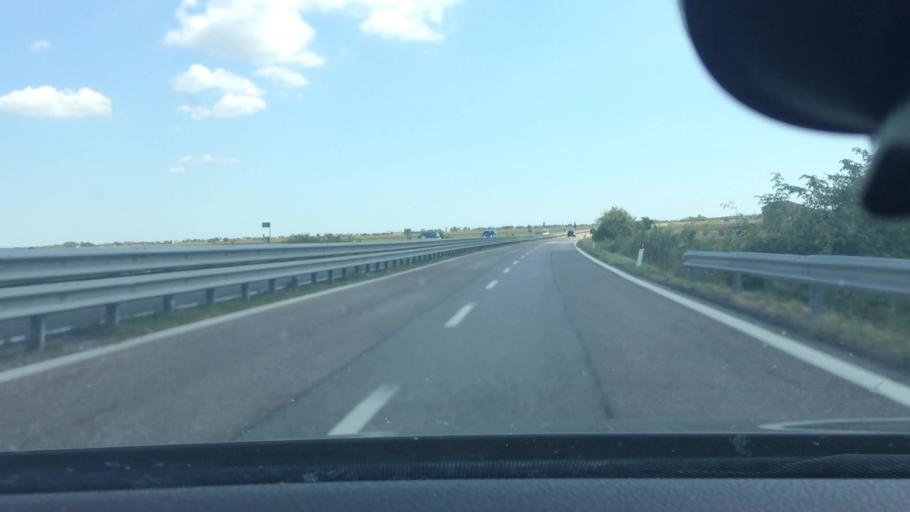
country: IT
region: Emilia-Romagna
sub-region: Provincia di Ferrara
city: Ostellato
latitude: 44.7562
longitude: 11.9663
